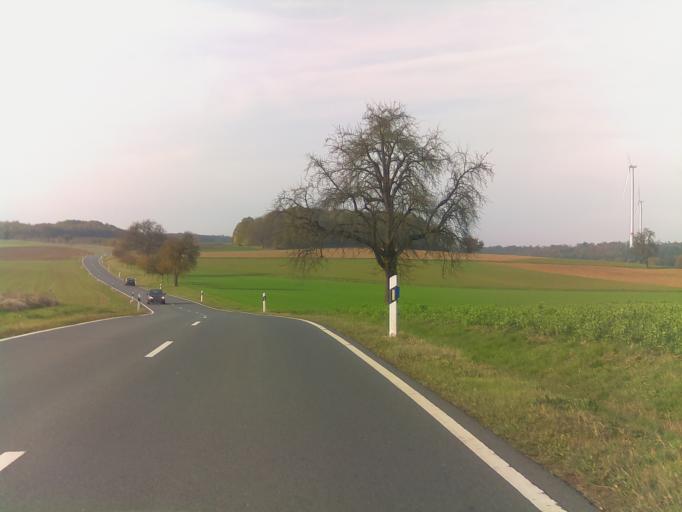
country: DE
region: Baden-Wuerttemberg
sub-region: Karlsruhe Region
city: Rosenberg
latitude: 49.4023
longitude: 9.4975
